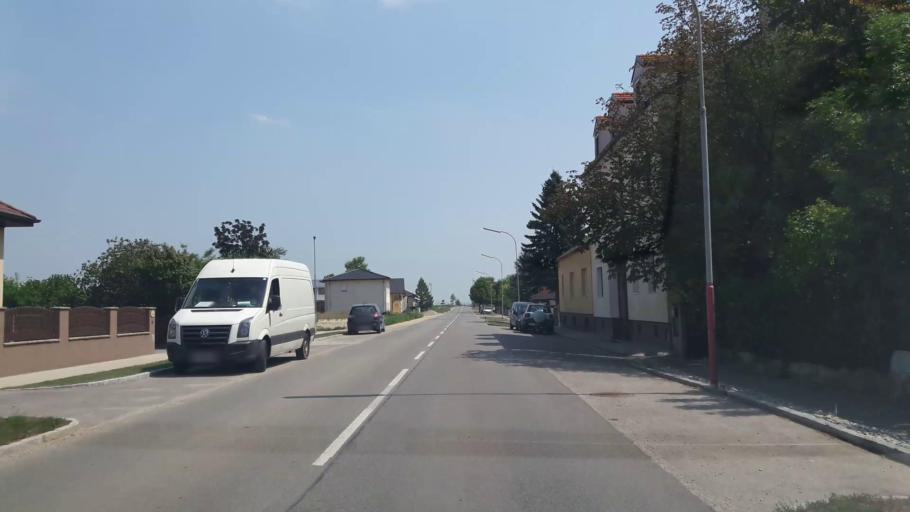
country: AT
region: Lower Austria
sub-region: Politischer Bezirk Bruck an der Leitha
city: Trautmannsdorf an der Leitha
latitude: 48.0226
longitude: 16.6497
